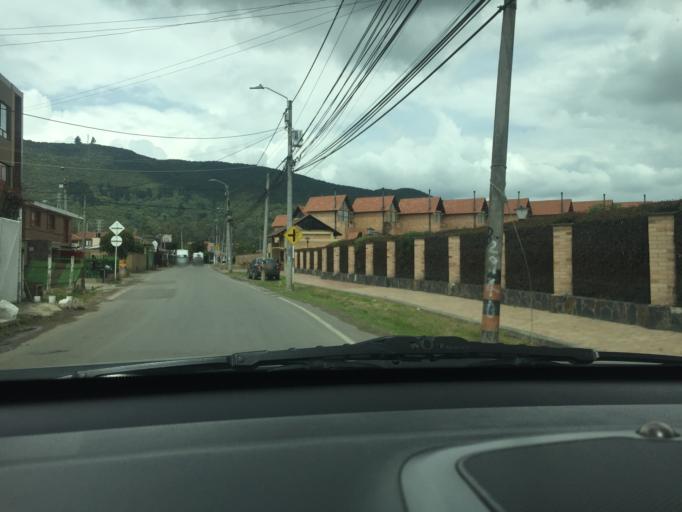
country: CO
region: Cundinamarca
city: Chia
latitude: 4.8750
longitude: -74.0689
